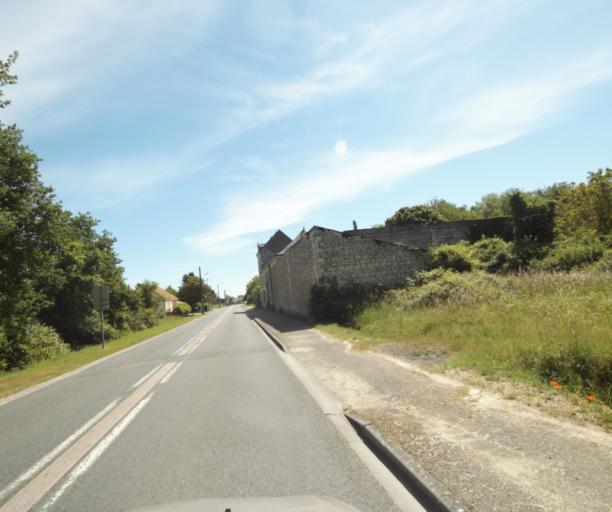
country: FR
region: Centre
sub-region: Departement d'Indre-et-Loire
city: Ligre
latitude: 47.1352
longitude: 0.3023
